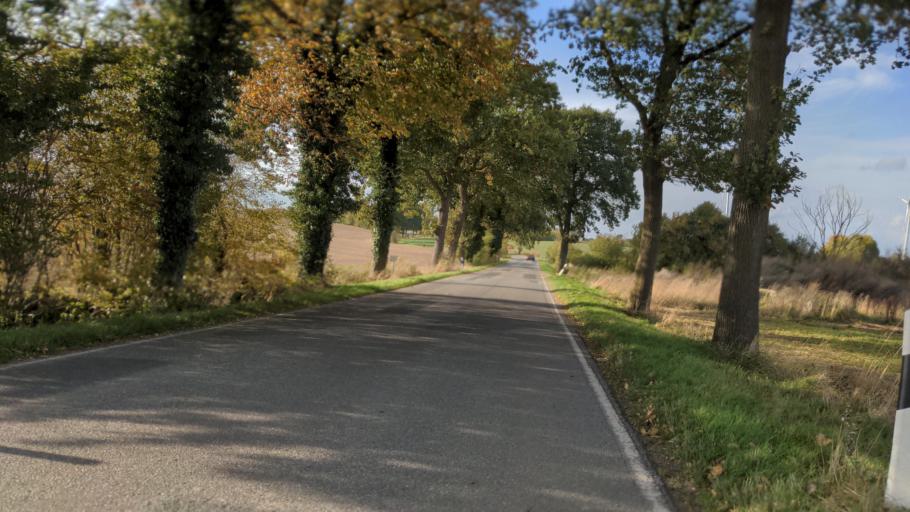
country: DE
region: Schleswig-Holstein
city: Monkhagen
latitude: 53.9493
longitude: 10.5532
